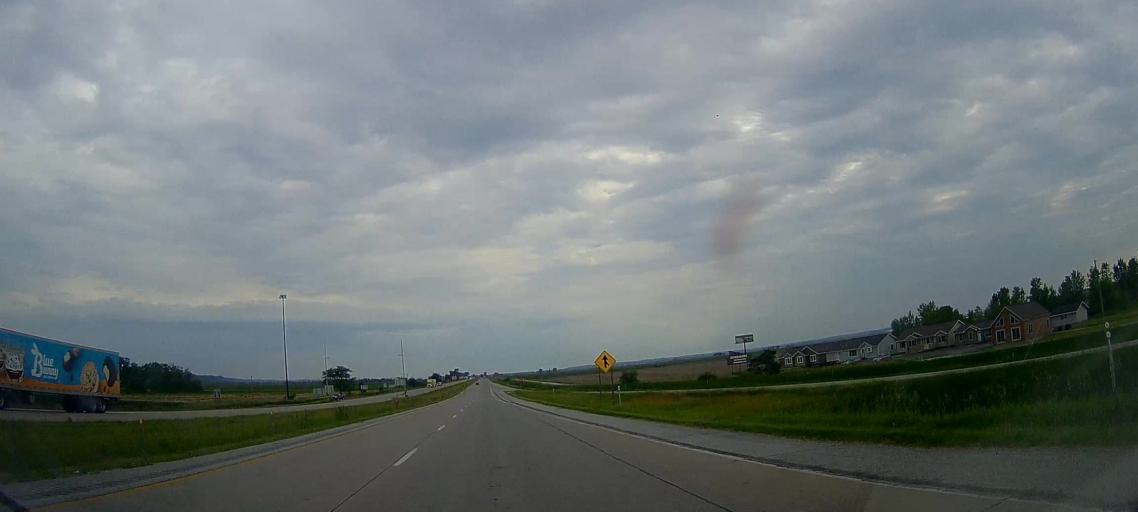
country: US
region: Iowa
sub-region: Harrison County
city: Missouri Valley
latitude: 41.5482
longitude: -95.9178
